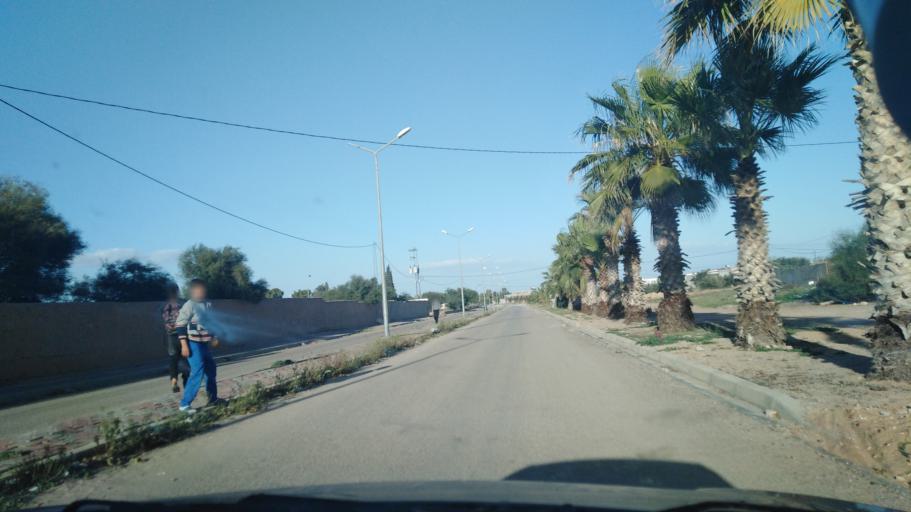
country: TN
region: Al Mahdiyah
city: Shurban
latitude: 34.9634
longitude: 10.3694
